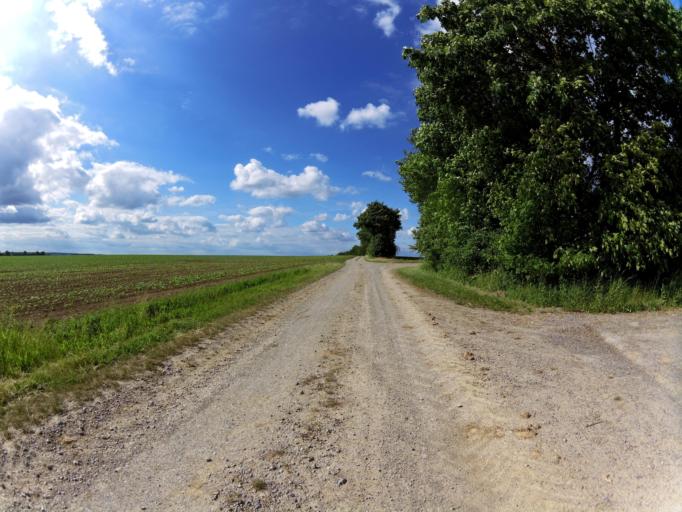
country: DE
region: Bavaria
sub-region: Regierungsbezirk Unterfranken
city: Gaukonigshofen
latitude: 49.6601
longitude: 10.0245
